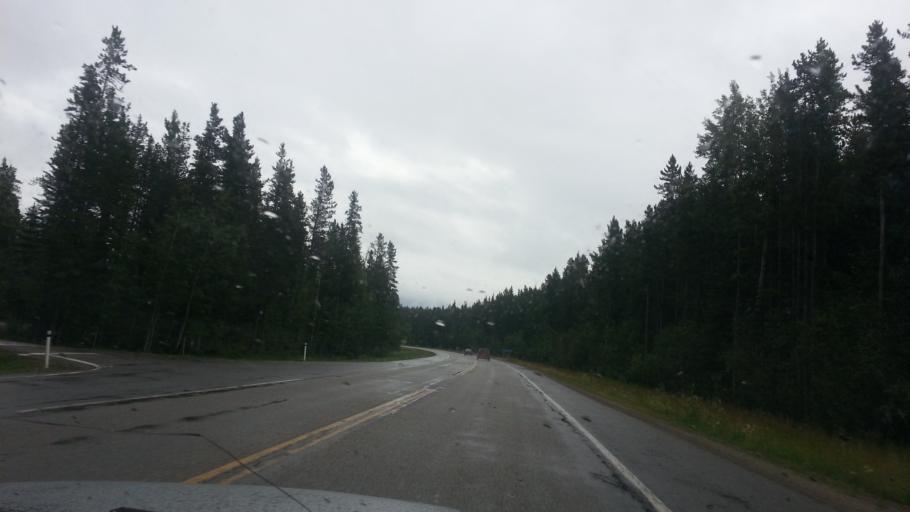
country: CA
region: Alberta
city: Cochrane
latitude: 50.9114
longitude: -114.6363
